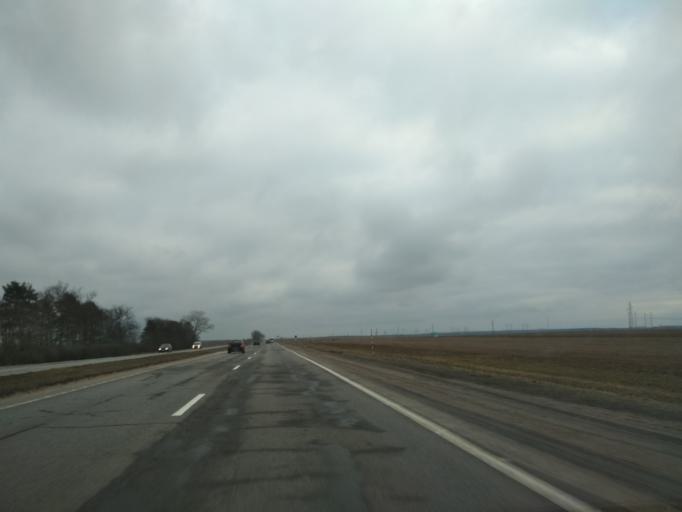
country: BY
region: Minsk
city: Dukora
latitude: 53.6962
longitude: 27.8932
